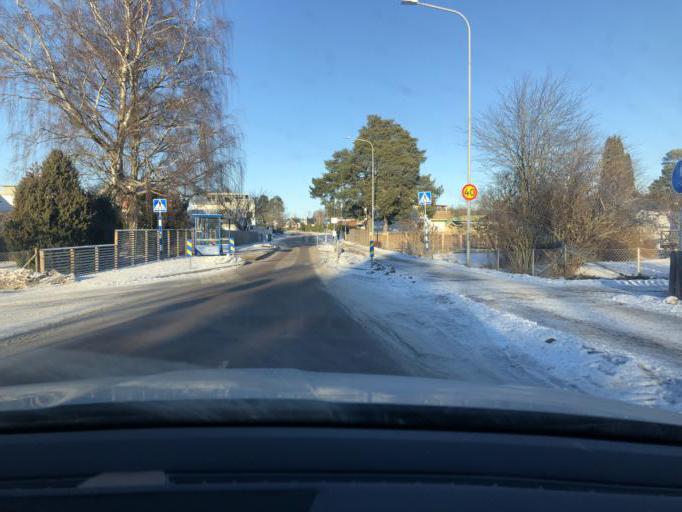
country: SE
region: Vaestmanland
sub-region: Vasteras
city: Hokasen
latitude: 59.6631
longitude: 16.5916
